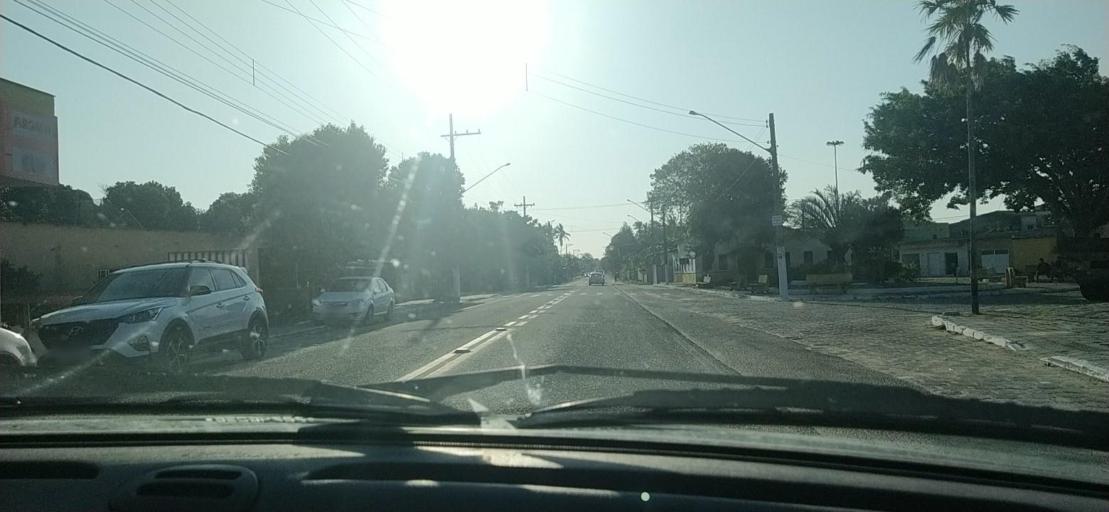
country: BR
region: Espirito Santo
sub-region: Conceicao Da Barra
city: Conceicao da Barra
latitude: -18.5681
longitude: -39.7525
